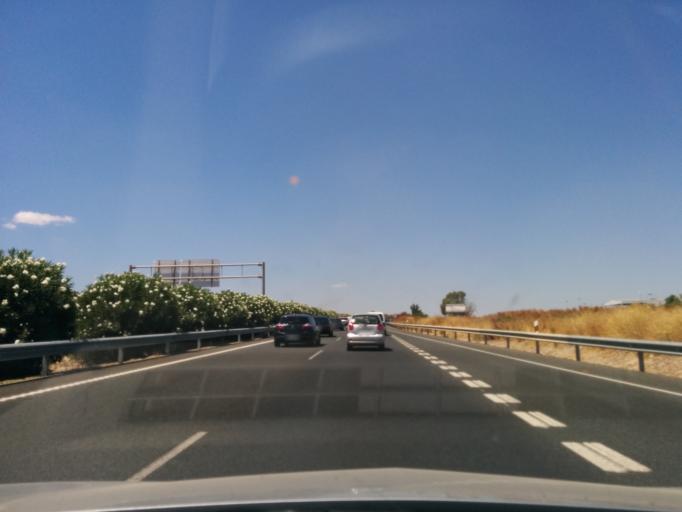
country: ES
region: Andalusia
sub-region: Provincia de Sevilla
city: Carrion de los Cespedes
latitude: 37.3612
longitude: -6.2760
